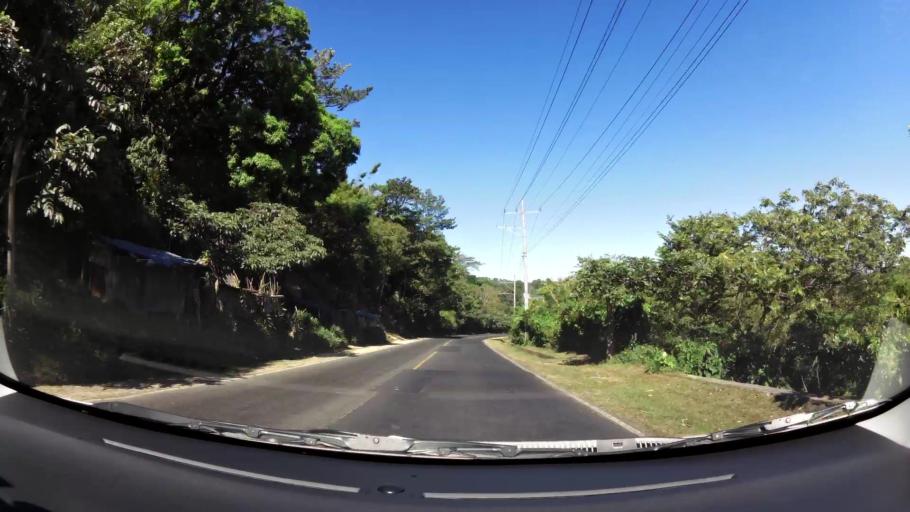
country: SV
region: Ahuachapan
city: Concepcion de Ataco
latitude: 13.8633
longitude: -89.8491
